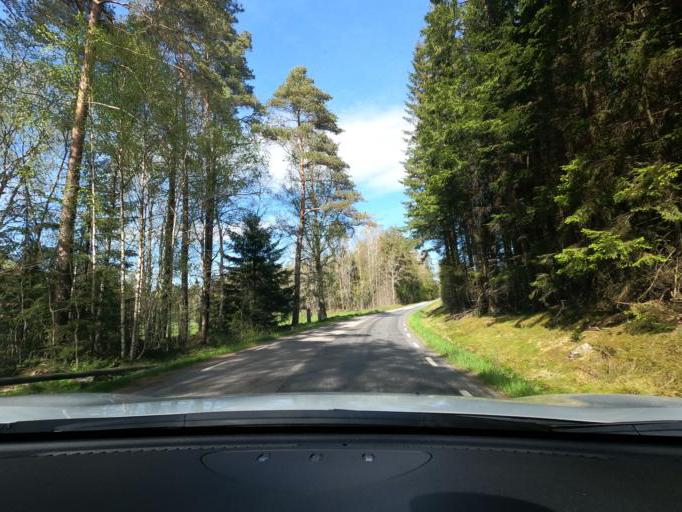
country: SE
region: Vaestra Goetaland
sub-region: Marks Kommun
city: Horred
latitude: 57.4447
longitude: 12.4339
